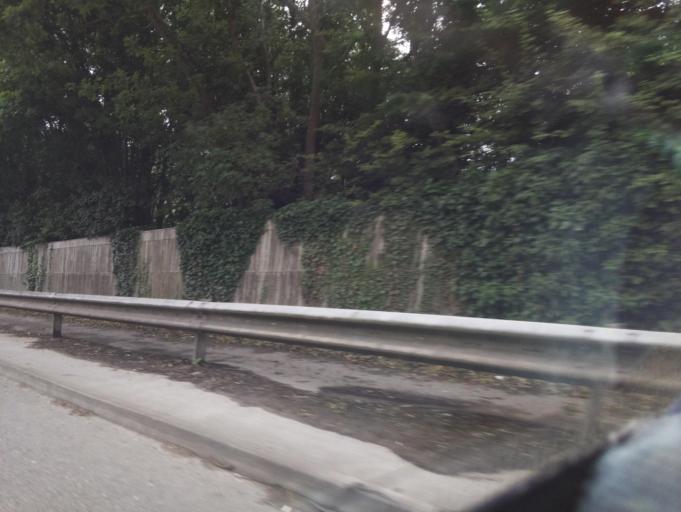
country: GB
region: England
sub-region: Nottinghamshire
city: Radcliffe on Trent
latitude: 52.9665
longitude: -1.0703
